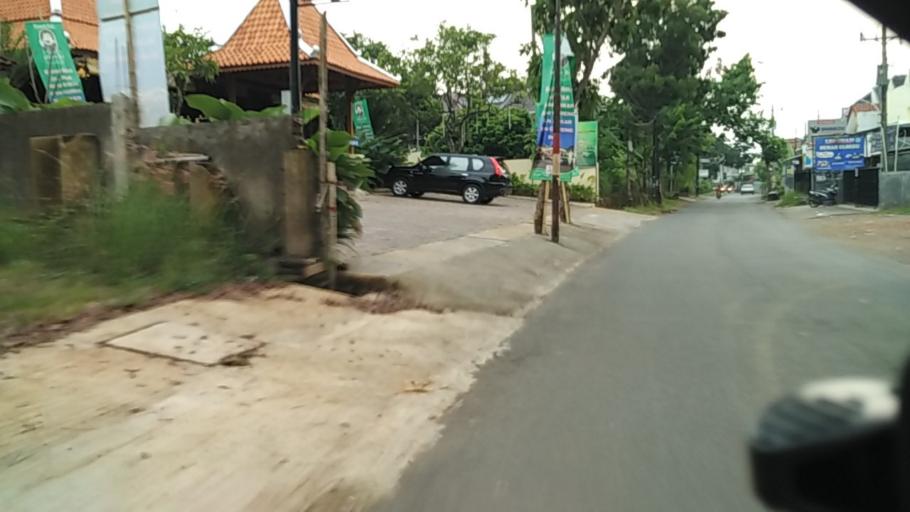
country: ID
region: Central Java
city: Semarang
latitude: -7.0611
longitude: 110.4357
